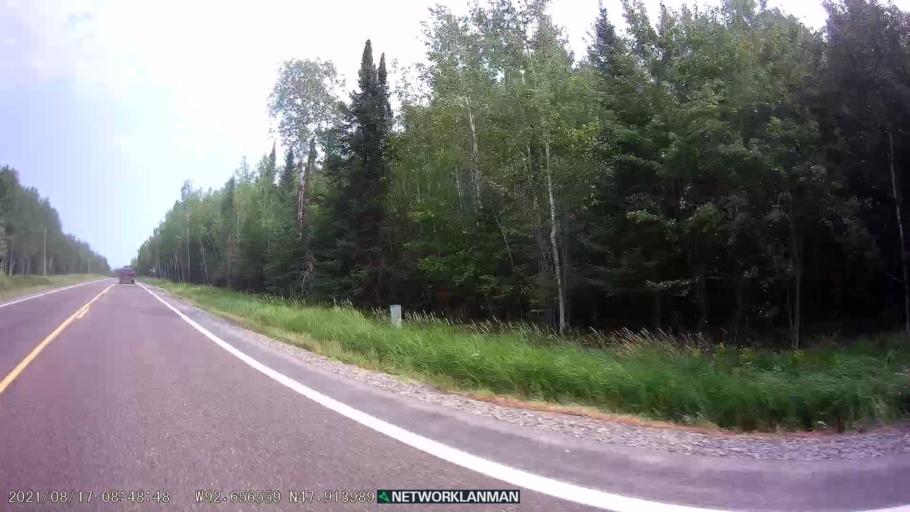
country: US
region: Minnesota
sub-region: Saint Louis County
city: Mountain Iron
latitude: 47.9142
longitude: -92.6566
